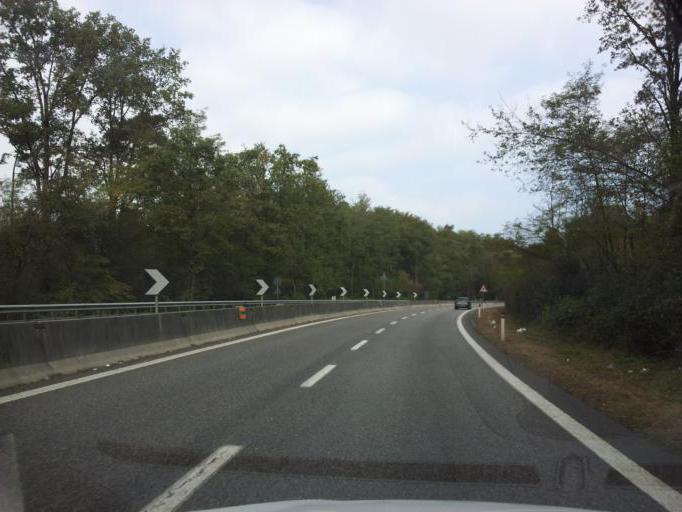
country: IT
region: Lombardy
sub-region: Provincia di Varese
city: Vergiate
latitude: 45.7252
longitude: 8.6780
